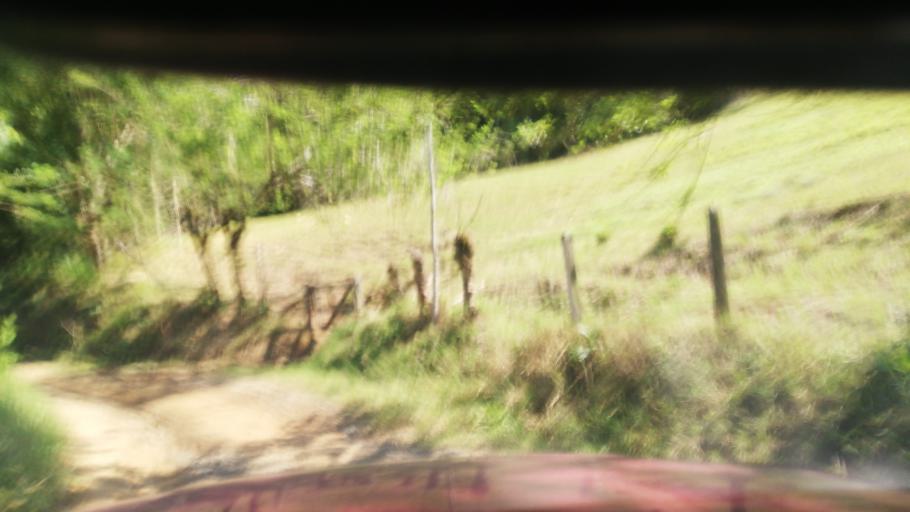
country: CO
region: Risaralda
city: Balboa
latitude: 4.9015
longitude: -75.9390
